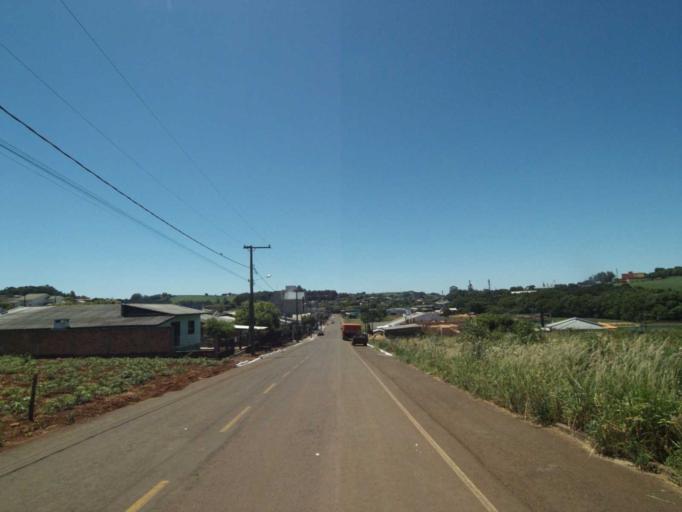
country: BR
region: Parana
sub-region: Coronel Vivida
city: Coronel Vivida
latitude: -25.9826
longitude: -52.8136
